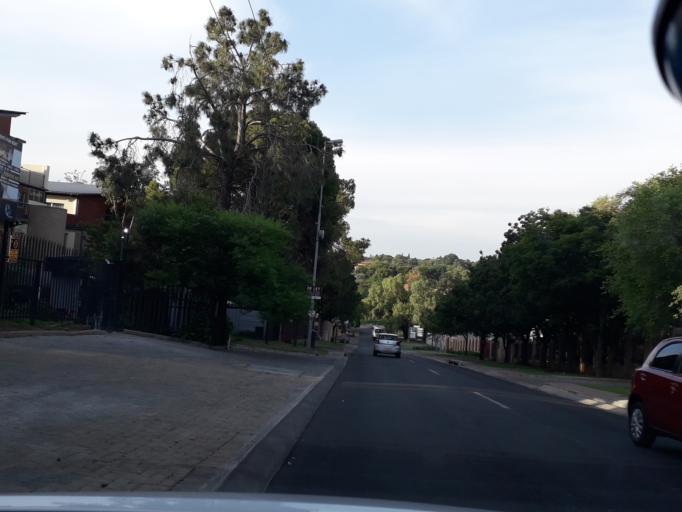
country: ZA
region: Gauteng
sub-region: City of Johannesburg Metropolitan Municipality
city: Johannesburg
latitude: -26.0883
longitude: 28.0013
